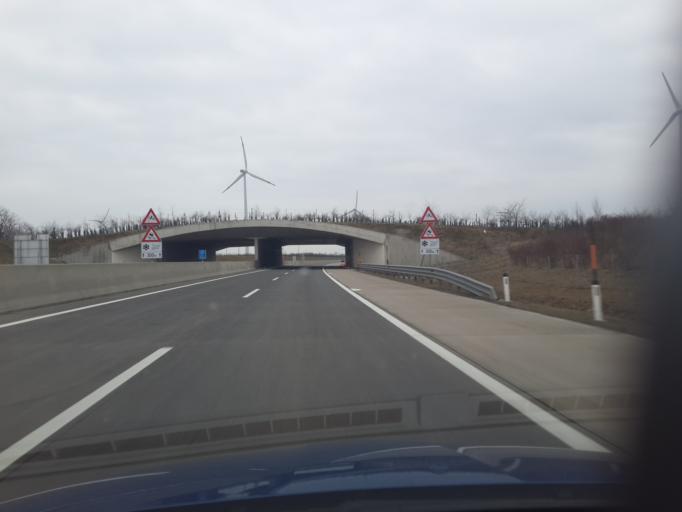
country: AT
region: Burgenland
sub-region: Politischer Bezirk Neusiedl am See
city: Potzneusiedl
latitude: 48.0279
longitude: 16.9265
